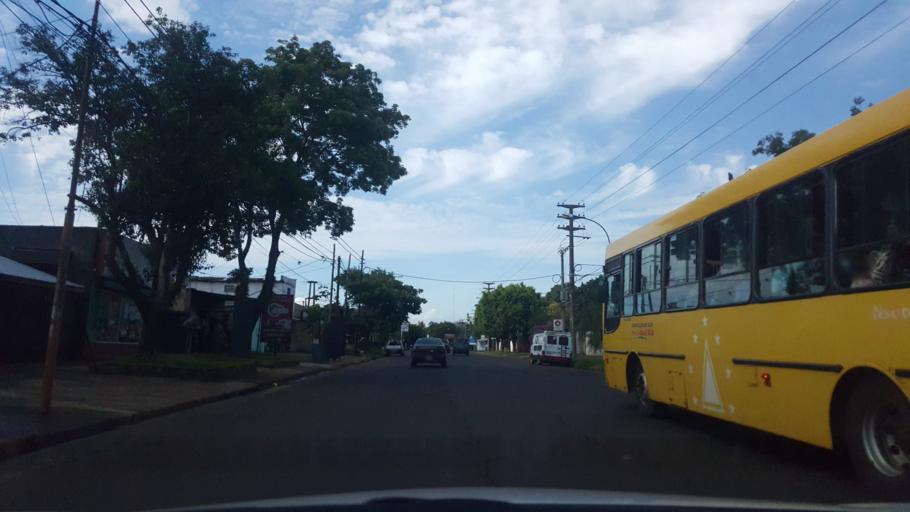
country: AR
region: Misiones
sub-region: Departamento de Capital
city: Posadas
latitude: -27.3933
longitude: -55.8973
